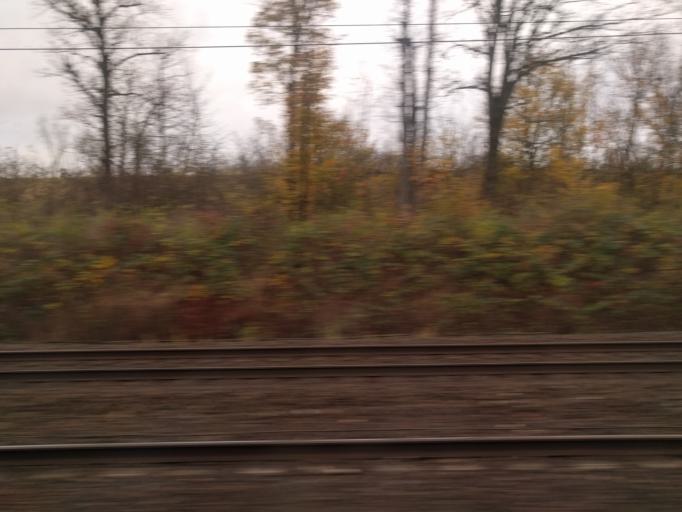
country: DK
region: Capital Region
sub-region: Hoje-Taastrup Kommune
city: Flong
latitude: 55.6445
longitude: 12.2277
